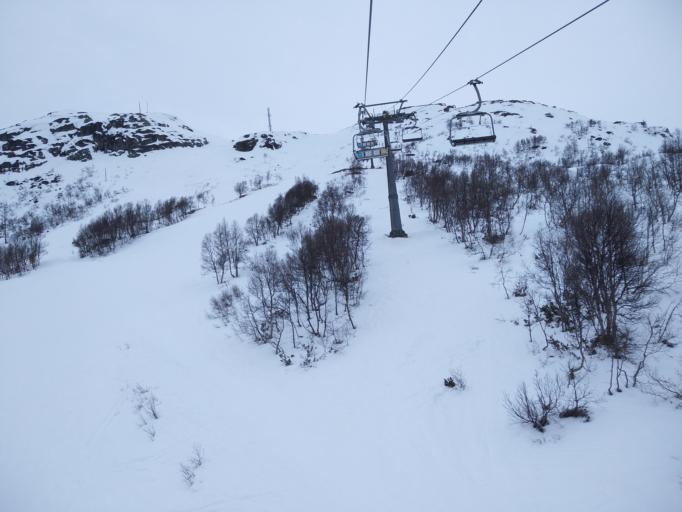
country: NO
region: Aust-Agder
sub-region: Bykle
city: Hovden
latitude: 59.5754
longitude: 7.3392
